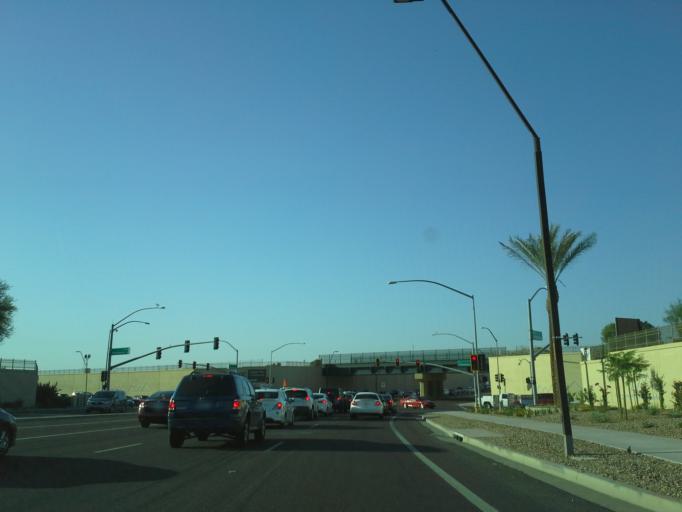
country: US
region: Arizona
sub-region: Maricopa County
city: Queen Creek
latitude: 33.2572
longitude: -111.6383
